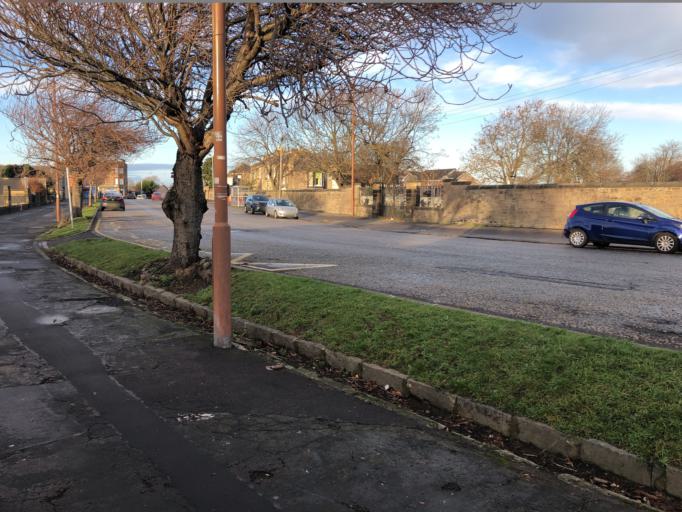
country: GB
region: Scotland
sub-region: West Lothian
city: Seafield
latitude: 55.9540
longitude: -3.1400
